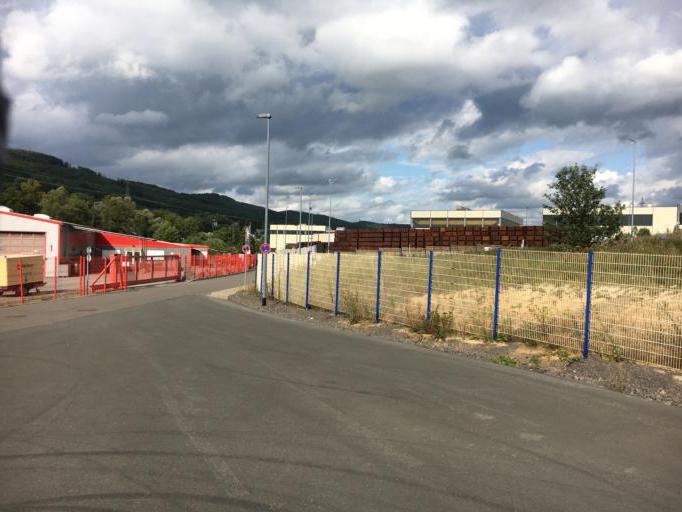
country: DE
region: North Rhine-Westphalia
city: Plettenberg
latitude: 51.1946
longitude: 7.8192
